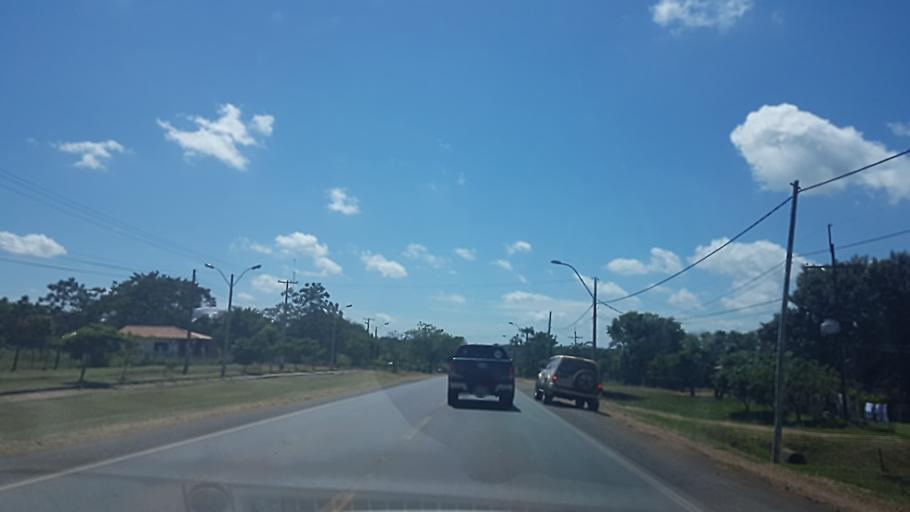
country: PY
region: Misiones
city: San Juan Bautista
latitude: -26.6719
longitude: -57.1287
